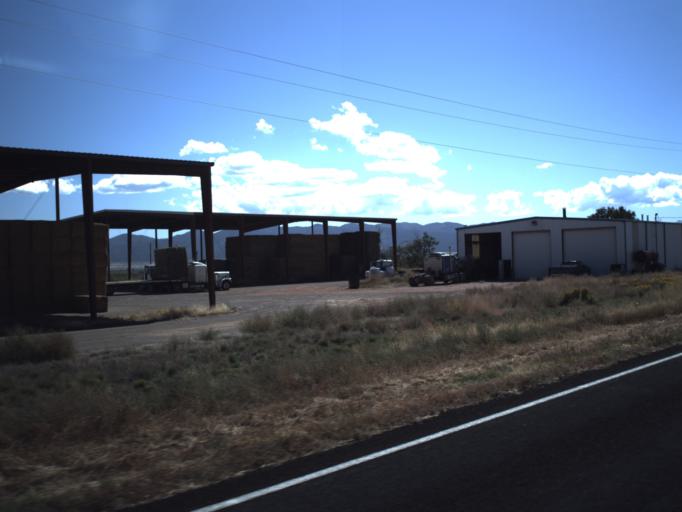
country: US
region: Utah
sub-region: Washington County
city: Enterprise
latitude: 37.6866
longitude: -113.6565
